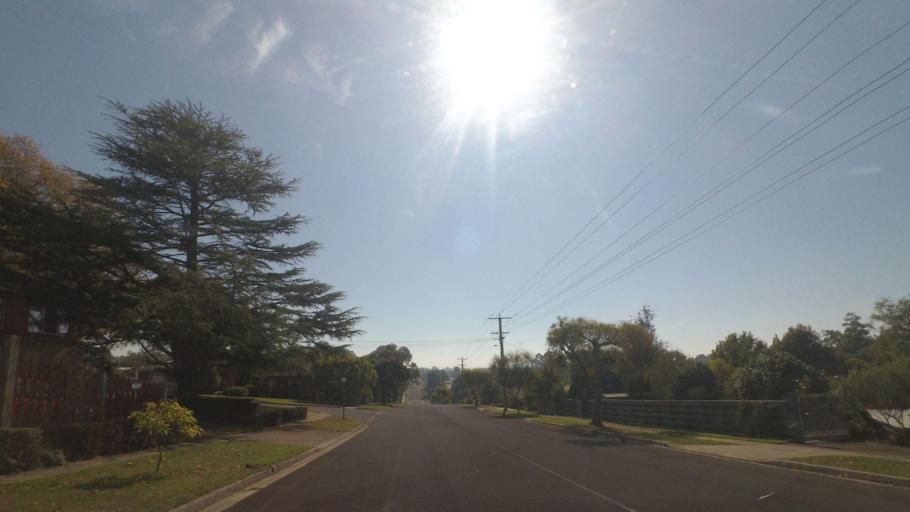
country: AU
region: Victoria
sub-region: Baw Baw
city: Warragul
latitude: -38.1472
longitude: 145.9424
